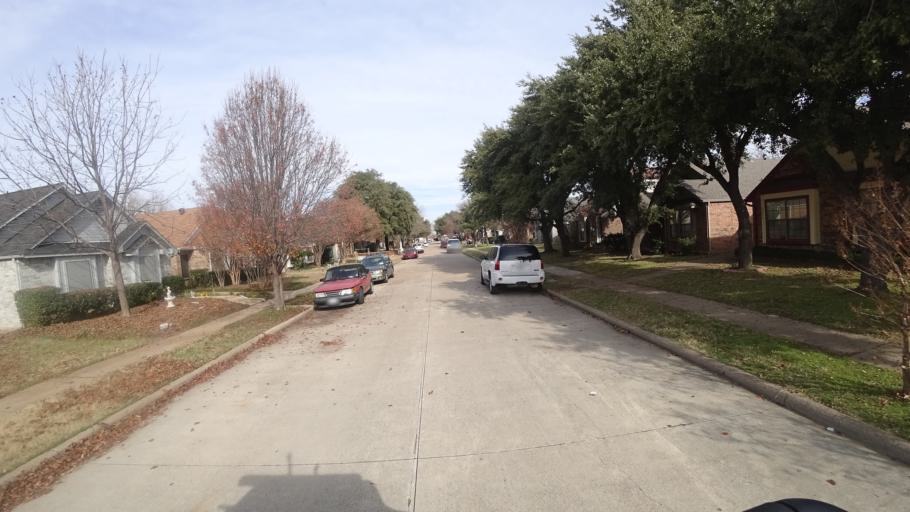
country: US
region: Texas
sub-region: Denton County
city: Highland Village
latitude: 33.0742
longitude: -97.0352
